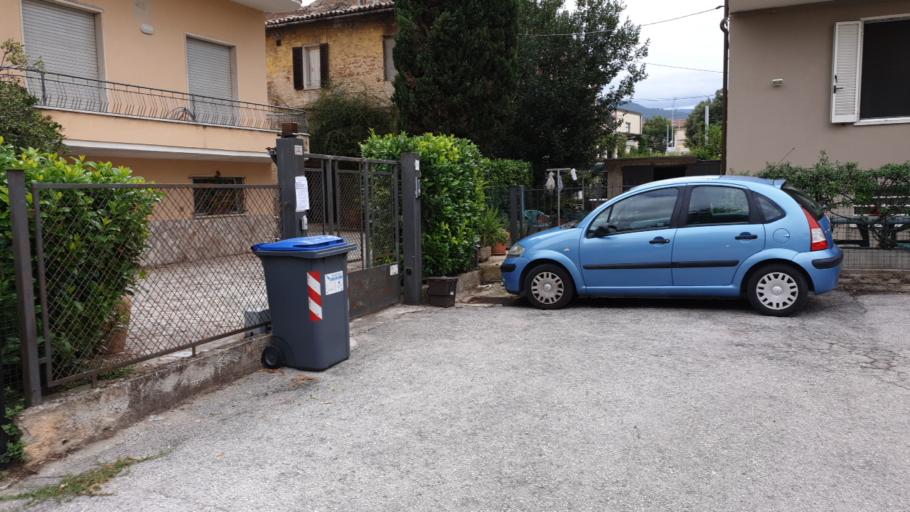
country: IT
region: Umbria
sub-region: Provincia di Perugia
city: Foligno
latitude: 42.9602
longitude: 12.7110
